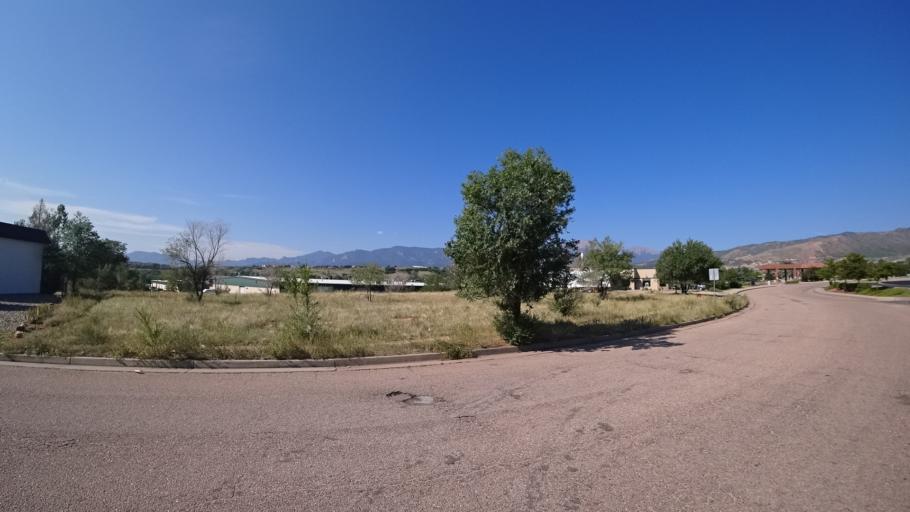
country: US
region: Colorado
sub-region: El Paso County
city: Colorado Springs
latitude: 38.8956
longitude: -104.8449
